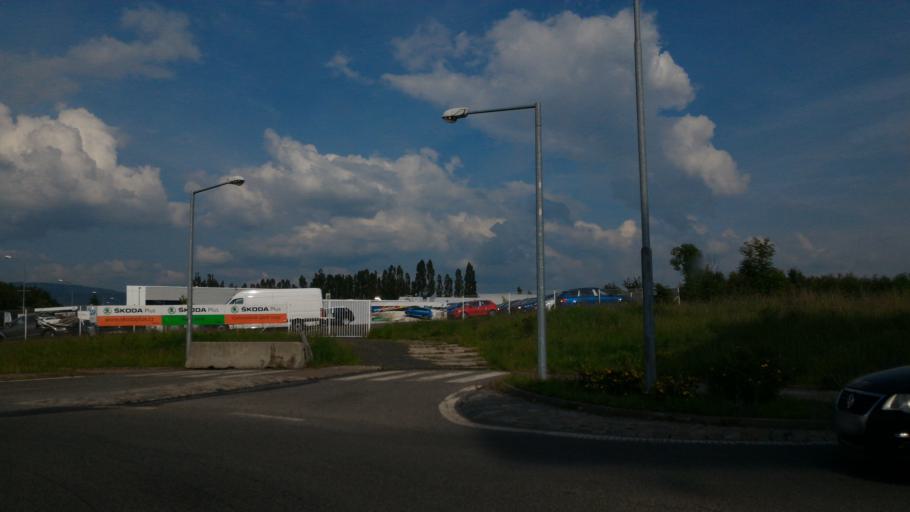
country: CZ
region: Liberecky
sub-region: Okres Liberec
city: Liberec
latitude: 50.7434
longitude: 15.0453
